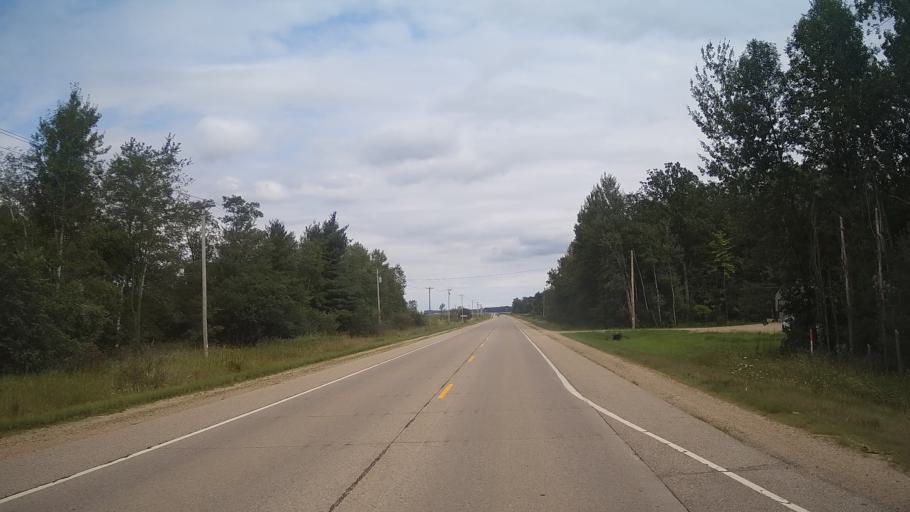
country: US
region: Wisconsin
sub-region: Waushara County
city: Redgranite
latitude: 44.0375
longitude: -89.0713
